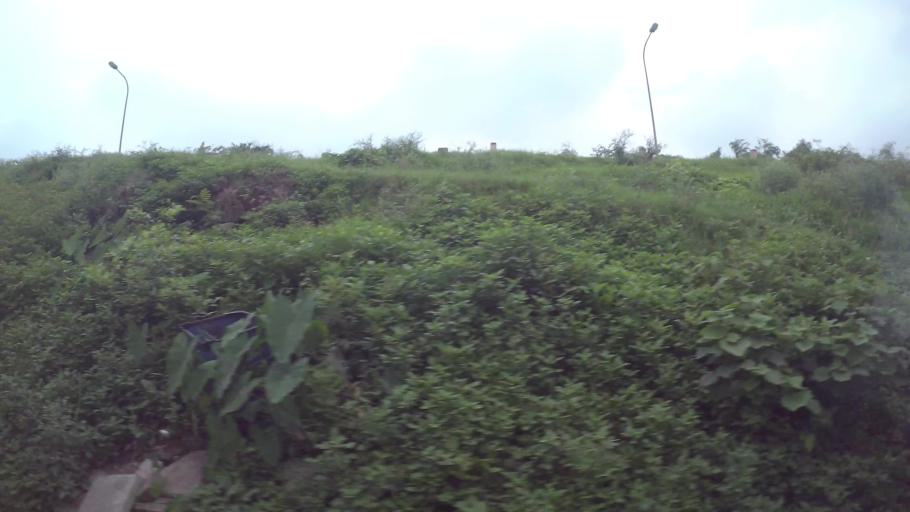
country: VN
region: Ha Noi
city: Trau Quy
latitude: 21.0518
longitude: 105.9241
